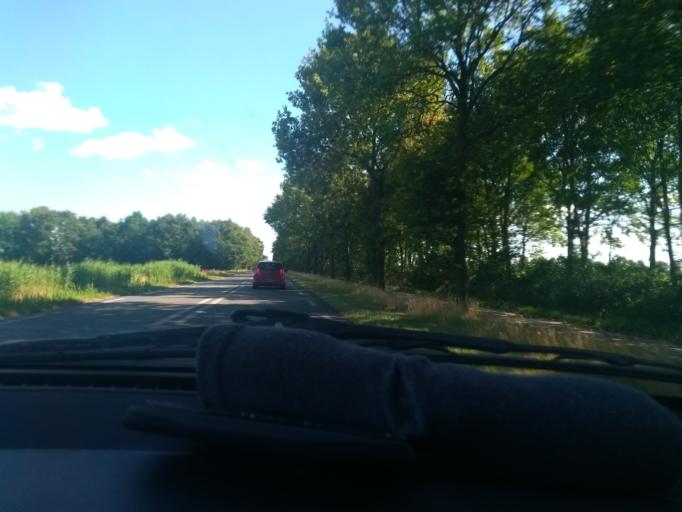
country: NL
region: Drenthe
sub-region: Gemeente Tynaarlo
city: Vries
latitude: 53.1331
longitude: 6.4991
